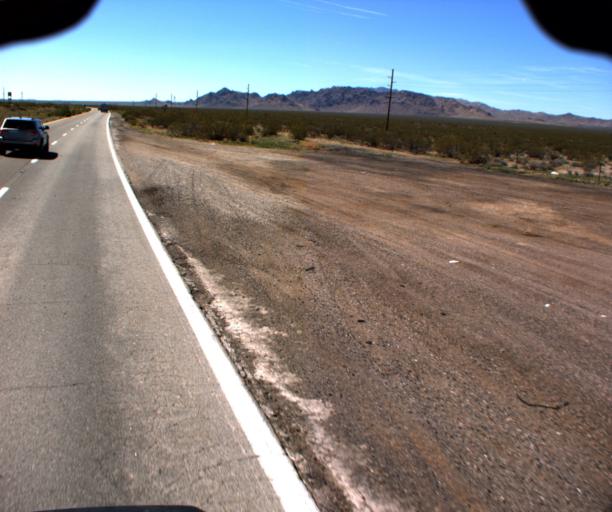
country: US
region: Arizona
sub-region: Mohave County
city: Dolan Springs
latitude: 35.6903
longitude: -114.4700
